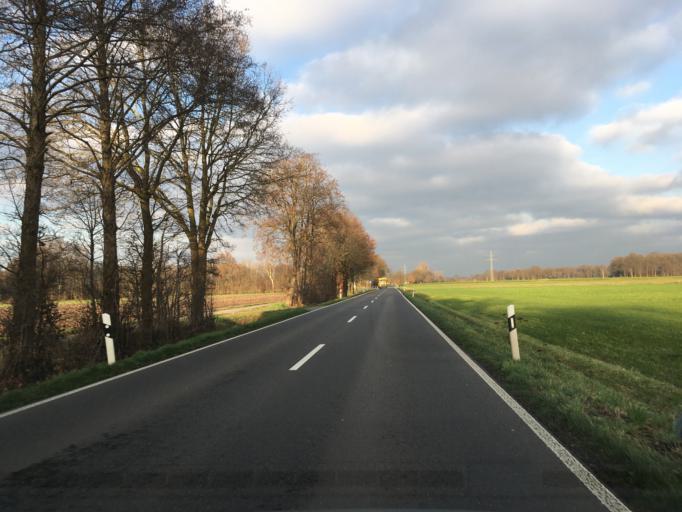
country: DE
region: North Rhine-Westphalia
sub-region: Regierungsbezirk Munster
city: Ahaus
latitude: 52.1388
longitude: 7.0083
